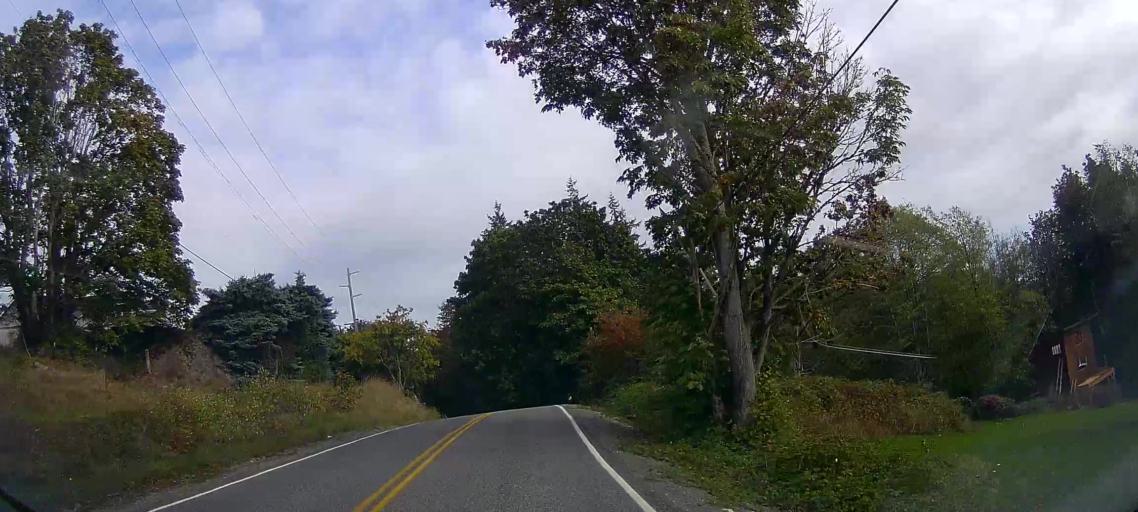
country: US
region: Washington
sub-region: Skagit County
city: Burlington
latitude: 48.4537
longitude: -122.2903
